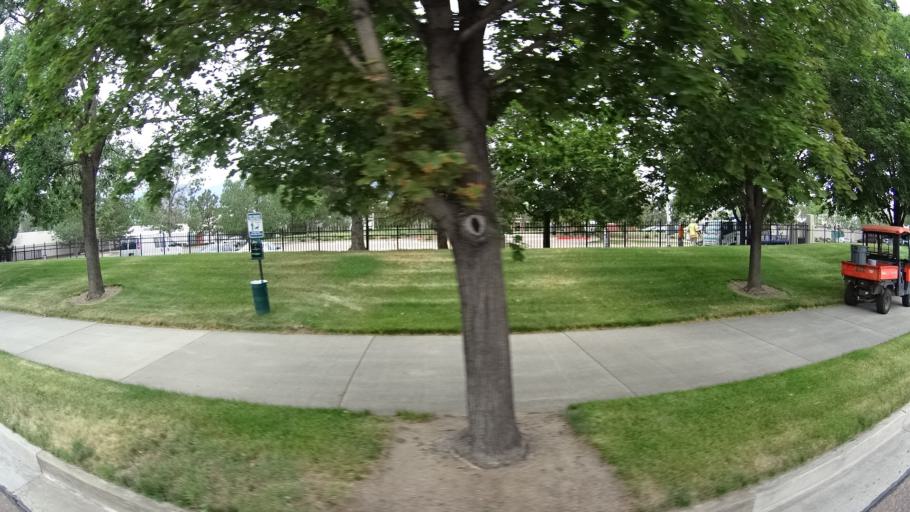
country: US
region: Colorado
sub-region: El Paso County
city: Colorado Springs
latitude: 38.8400
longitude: -104.7944
